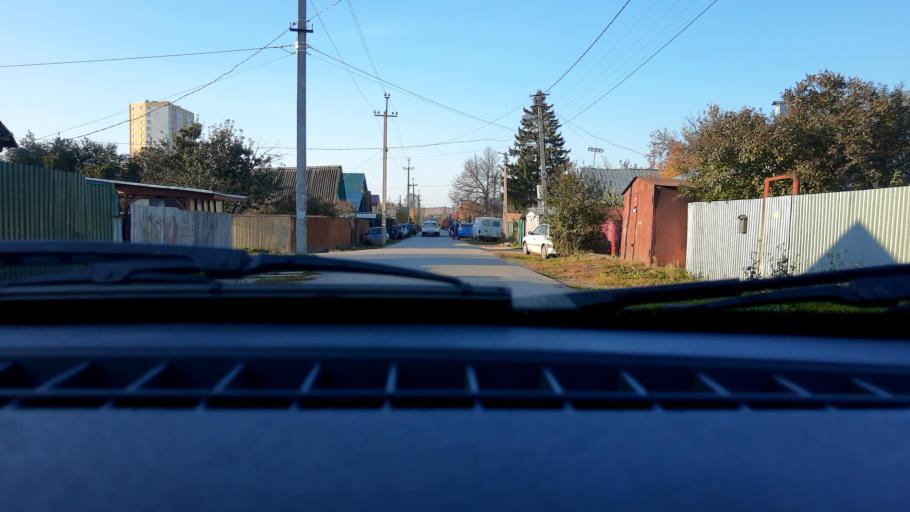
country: RU
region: Bashkortostan
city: Mikhaylovka
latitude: 54.7886
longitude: 55.8883
